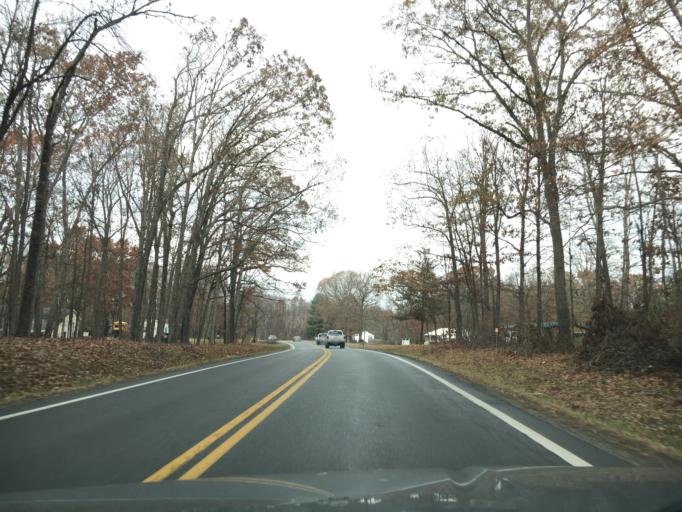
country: US
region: Virginia
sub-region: Prince Edward County
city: Farmville
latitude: 37.3715
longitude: -78.3687
